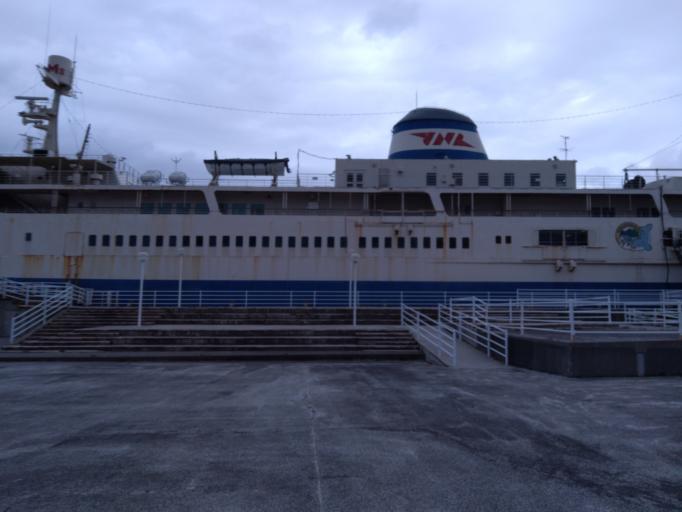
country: JP
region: Hokkaido
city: Hakodate
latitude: 41.7725
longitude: 140.7220
